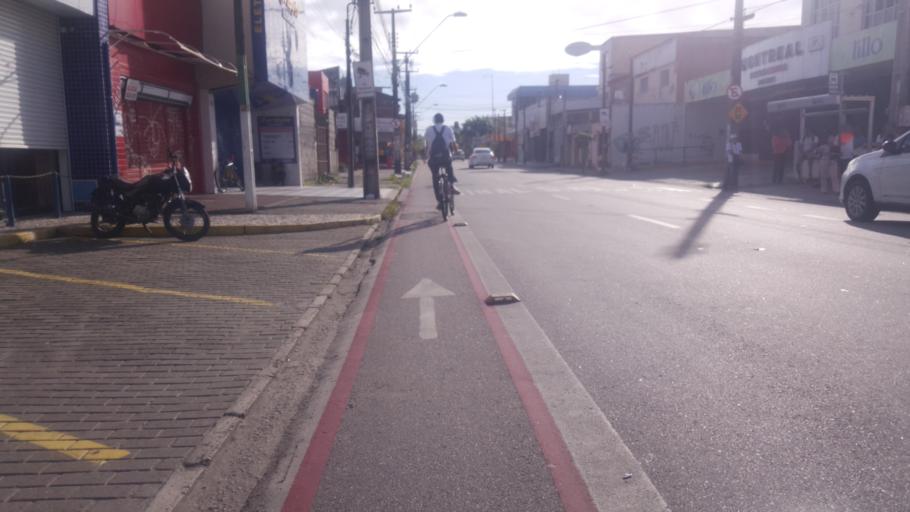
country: BR
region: Ceara
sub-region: Fortaleza
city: Fortaleza
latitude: -3.7589
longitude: -38.5437
